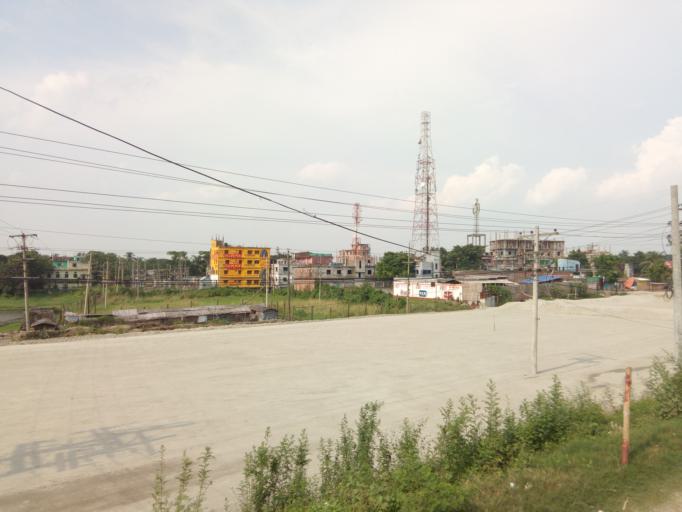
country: BD
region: Dhaka
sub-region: Dhaka
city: Dhaka
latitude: 23.6628
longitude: 90.3864
